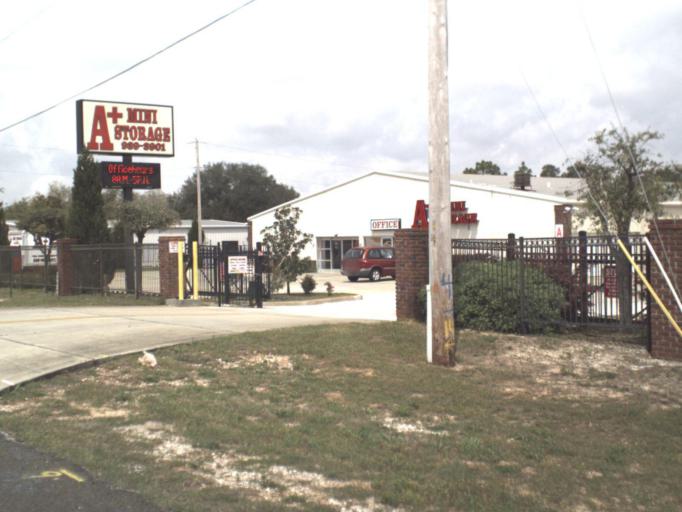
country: US
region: Florida
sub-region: Santa Rosa County
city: Holley
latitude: 30.4022
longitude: -86.9288
